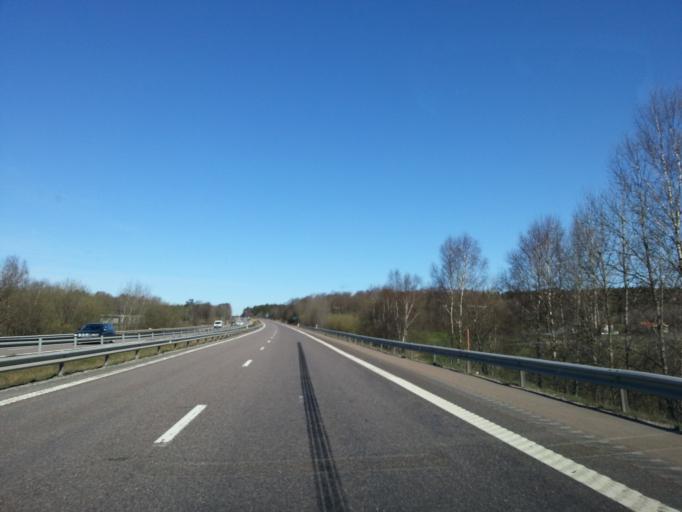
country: SE
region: Vaestra Goetaland
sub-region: Kungalvs Kommun
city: Kode
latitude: 57.9338
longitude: 11.8706
